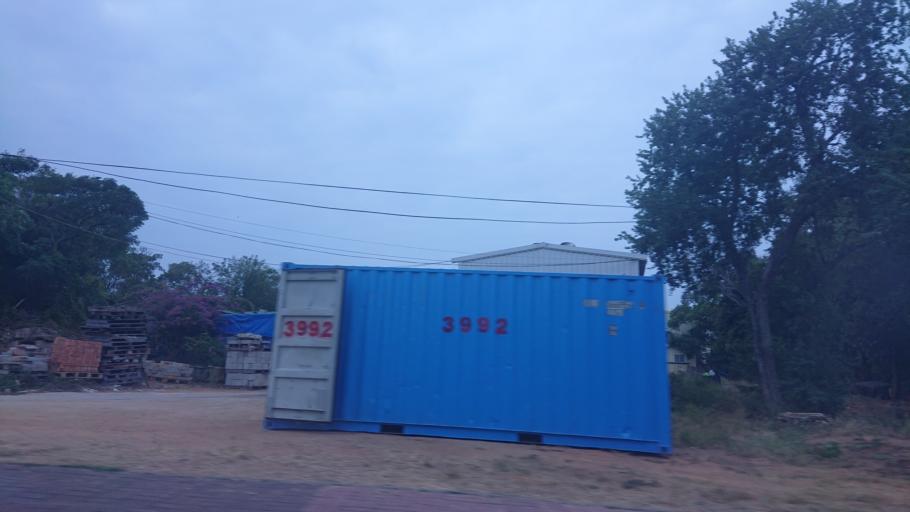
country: TW
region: Fukien
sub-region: Kinmen
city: Jincheng
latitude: 24.4365
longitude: 118.3126
